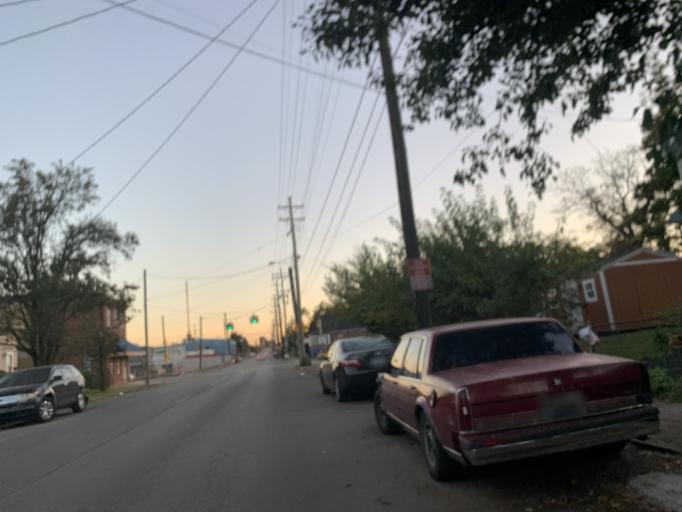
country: US
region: Kentucky
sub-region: Jefferson County
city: Louisville
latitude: 38.2372
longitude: -85.7784
